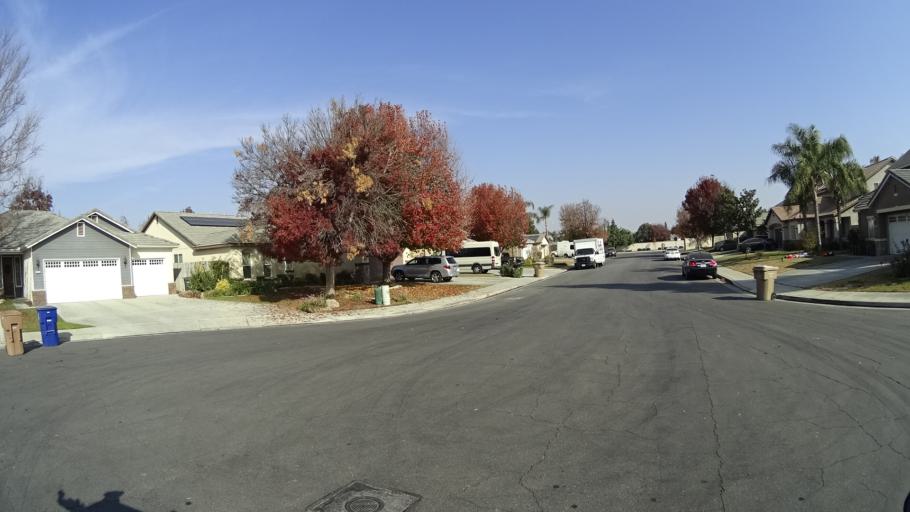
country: US
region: California
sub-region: Kern County
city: Greenacres
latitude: 35.4224
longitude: -119.1182
